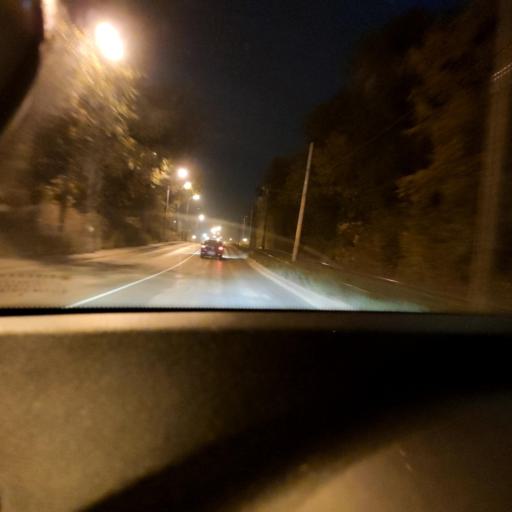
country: RU
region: Samara
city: Smyshlyayevka
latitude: 53.2254
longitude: 50.2836
